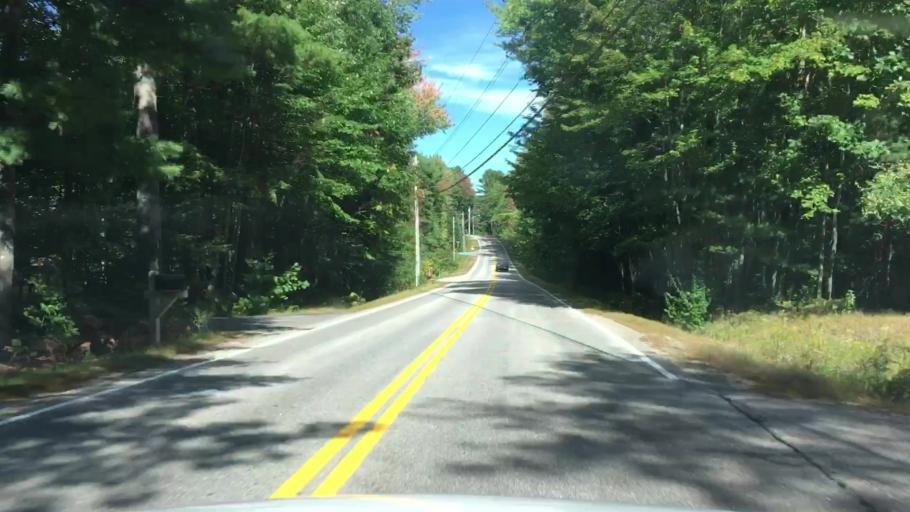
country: US
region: Maine
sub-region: Cumberland County
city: West Scarborough
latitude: 43.5999
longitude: -70.4251
